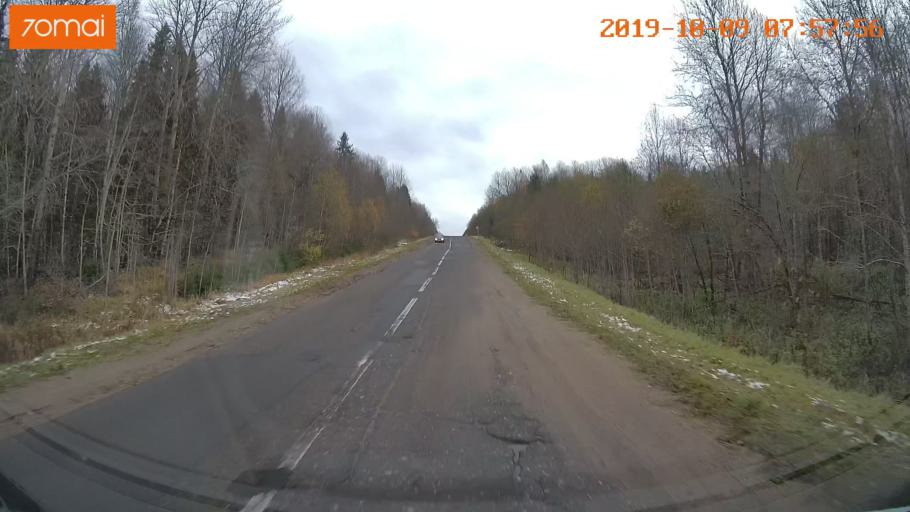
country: RU
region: Jaroslavl
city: Kukoboy
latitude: 58.6970
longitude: 39.9581
